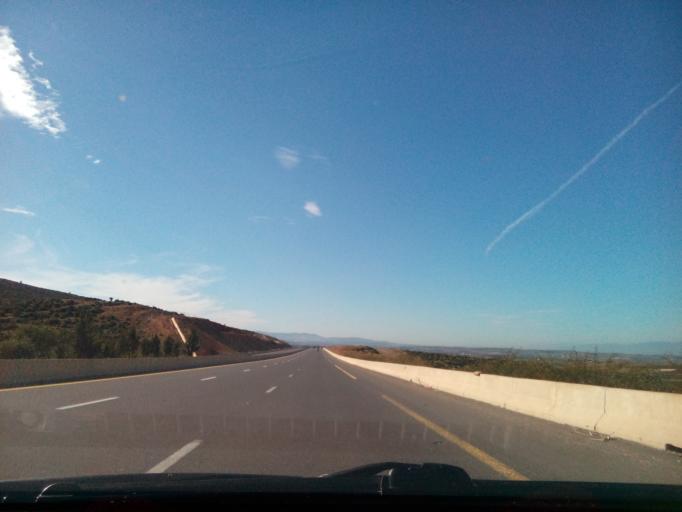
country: DZ
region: Tlemcen
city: Sidi Abdelli
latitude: 35.0167
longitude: -1.1504
